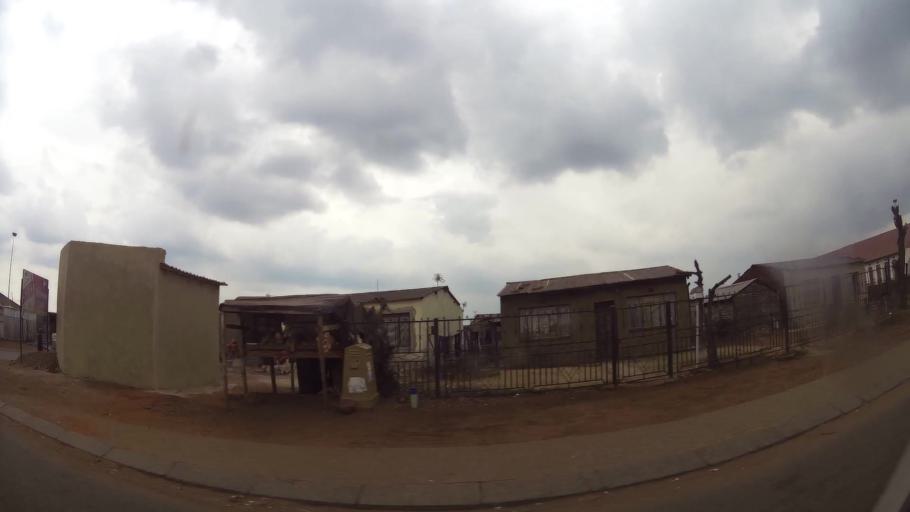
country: ZA
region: Gauteng
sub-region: Ekurhuleni Metropolitan Municipality
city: Germiston
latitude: -26.3546
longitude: 28.1498
